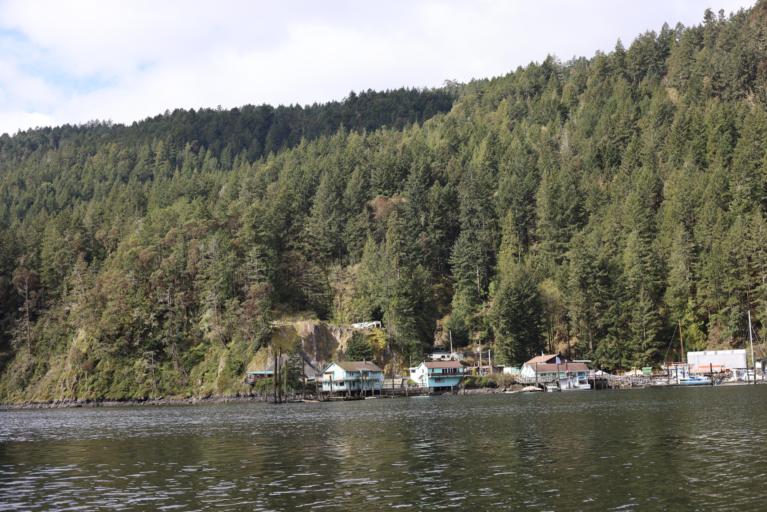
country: CA
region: British Columbia
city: Langford
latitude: 48.4974
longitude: -123.5488
